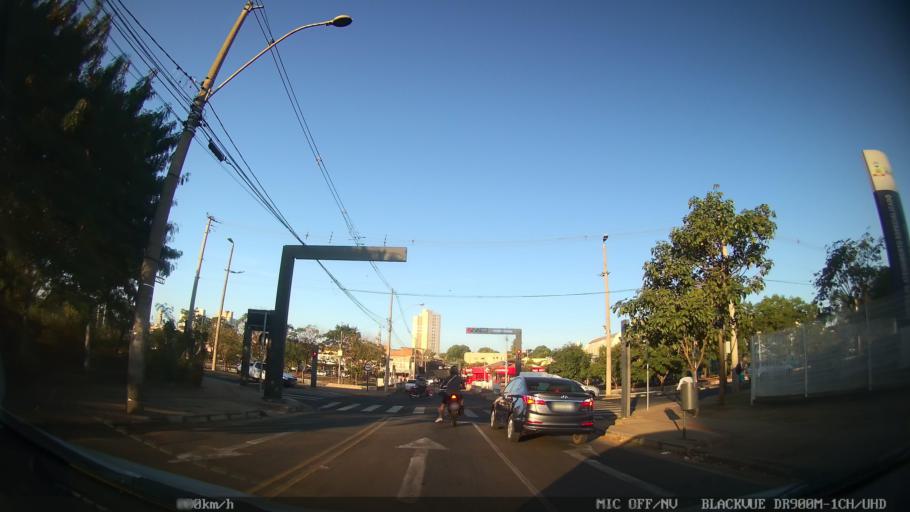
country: BR
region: Sao Paulo
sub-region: Sao Jose Do Rio Preto
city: Sao Jose do Rio Preto
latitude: -20.7966
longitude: -49.3772
